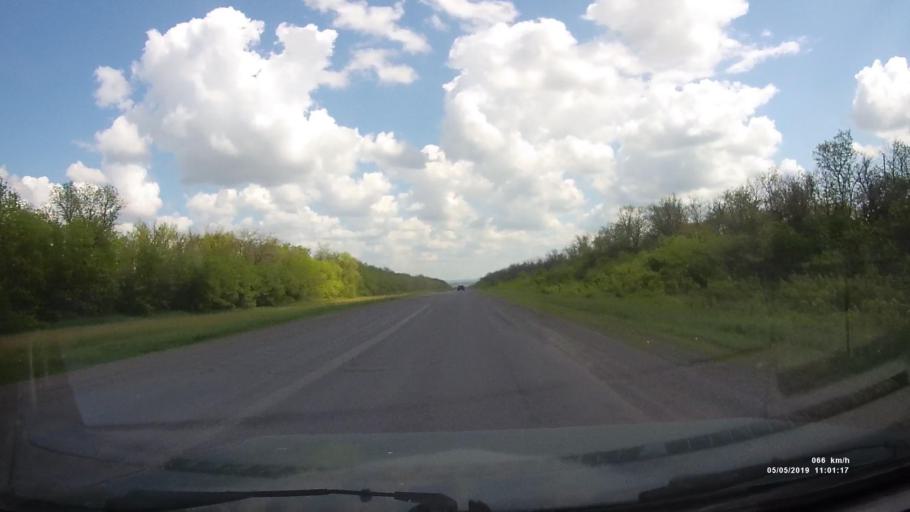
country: RU
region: Rostov
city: Ust'-Donetskiy
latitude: 47.6787
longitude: 40.8977
